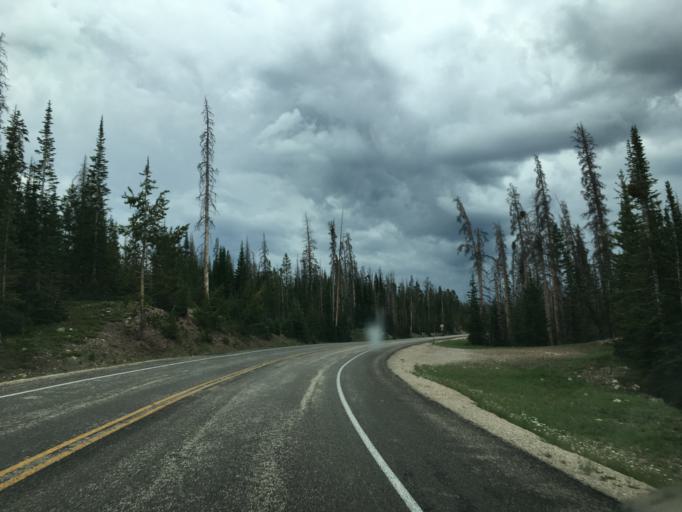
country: US
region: Utah
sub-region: Summit County
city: Kamas
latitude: 40.6844
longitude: -110.9293
